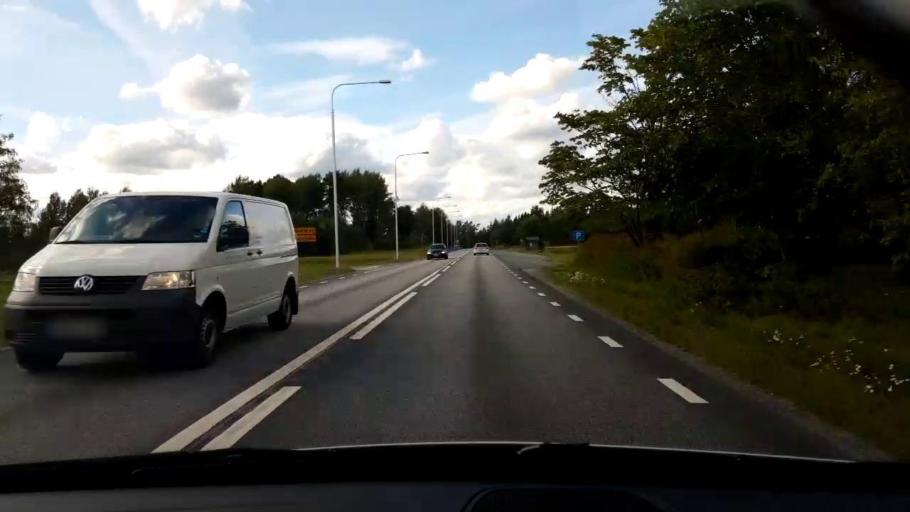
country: SE
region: Joenkoeping
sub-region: Savsjo Kommun
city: Vrigstad
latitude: 57.3607
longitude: 14.4575
